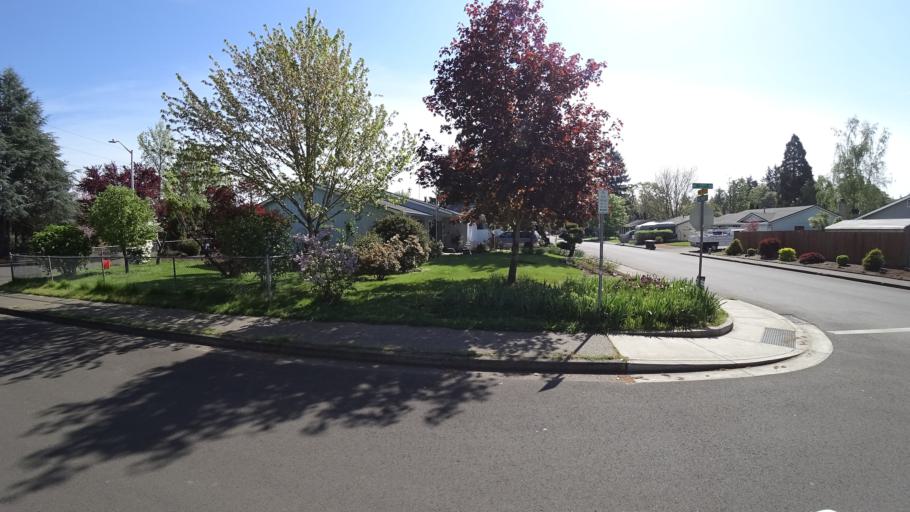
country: US
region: Oregon
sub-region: Washington County
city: Hillsboro
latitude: 45.5268
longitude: -122.9442
